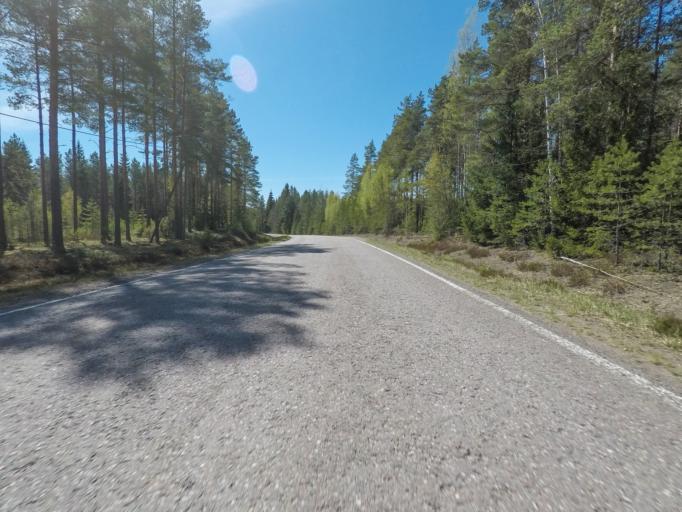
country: FI
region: Uusimaa
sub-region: Helsinki
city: Kaerkoelae
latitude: 60.5969
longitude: 23.8030
